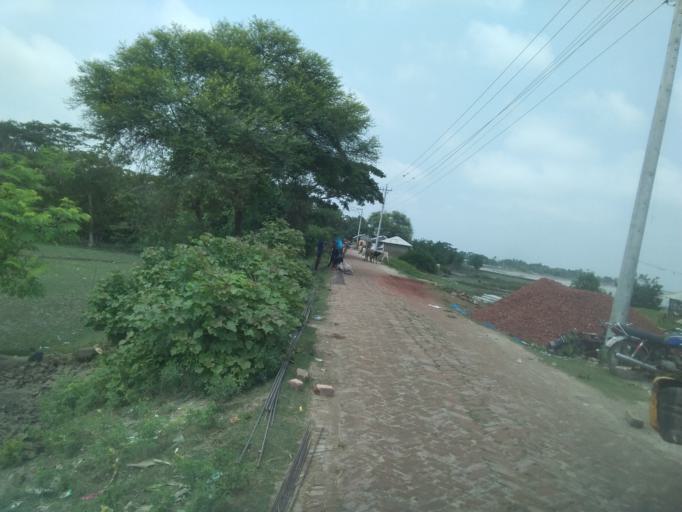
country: BD
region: Khulna
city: Phultala
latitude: 22.6432
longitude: 89.4307
